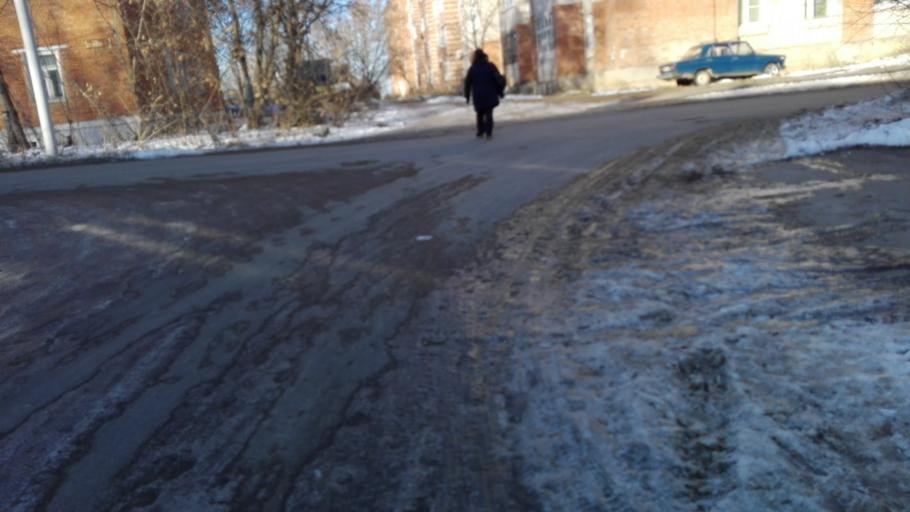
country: RU
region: Tula
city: Kosaya Gora
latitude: 54.1190
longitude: 37.5387
